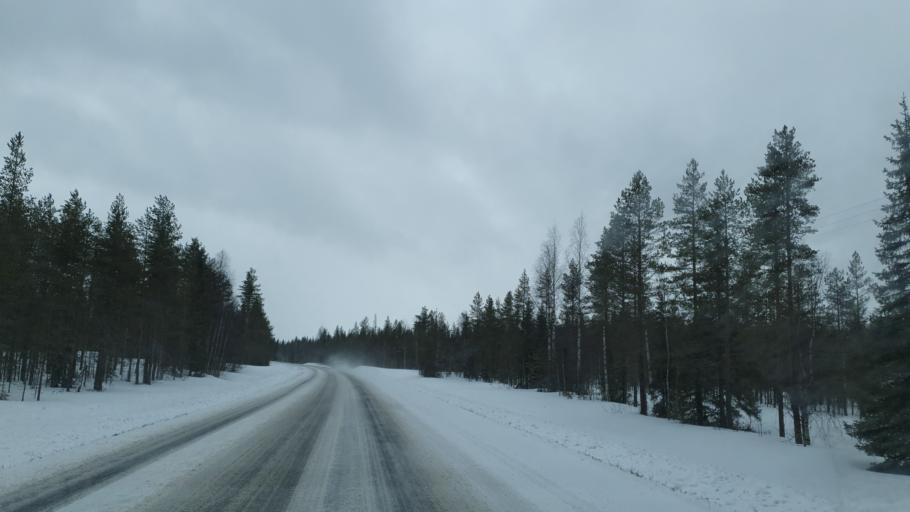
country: FI
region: Lapland
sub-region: Rovaniemi
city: Ranua
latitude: 66.1344
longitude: 26.2775
